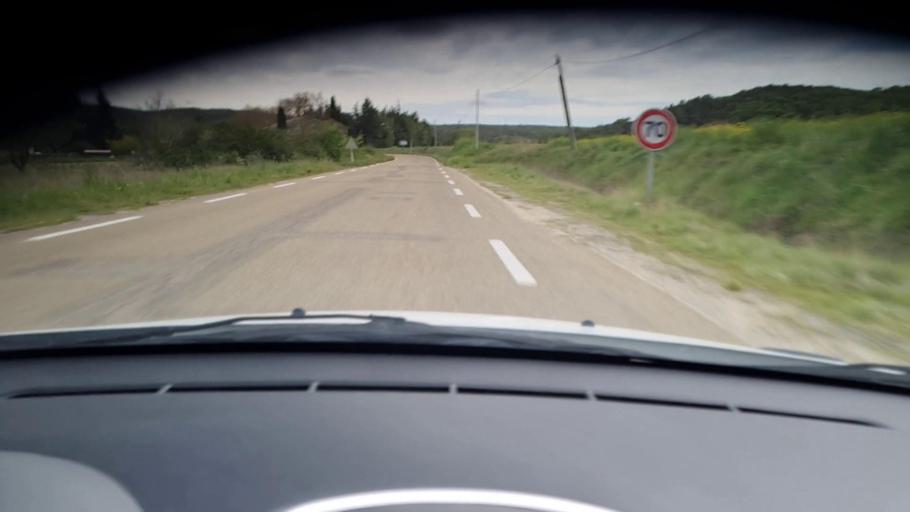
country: FR
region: Languedoc-Roussillon
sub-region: Departement du Gard
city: Blauzac
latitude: 43.9540
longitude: 4.3800
